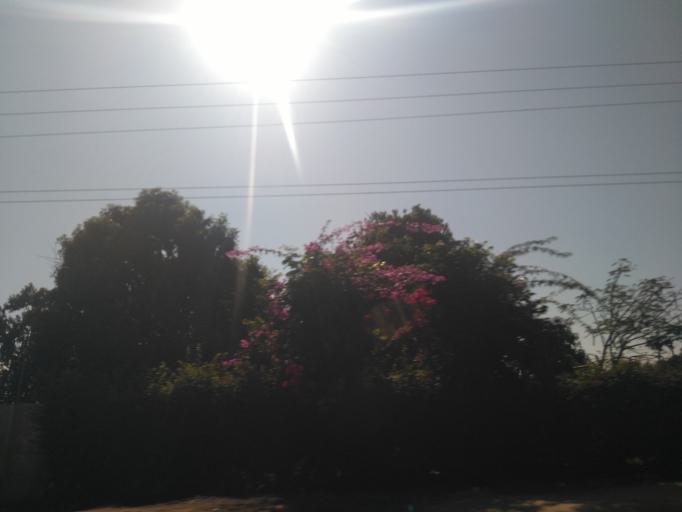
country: TZ
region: Dodoma
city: Dodoma
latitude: -6.1363
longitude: 35.7467
